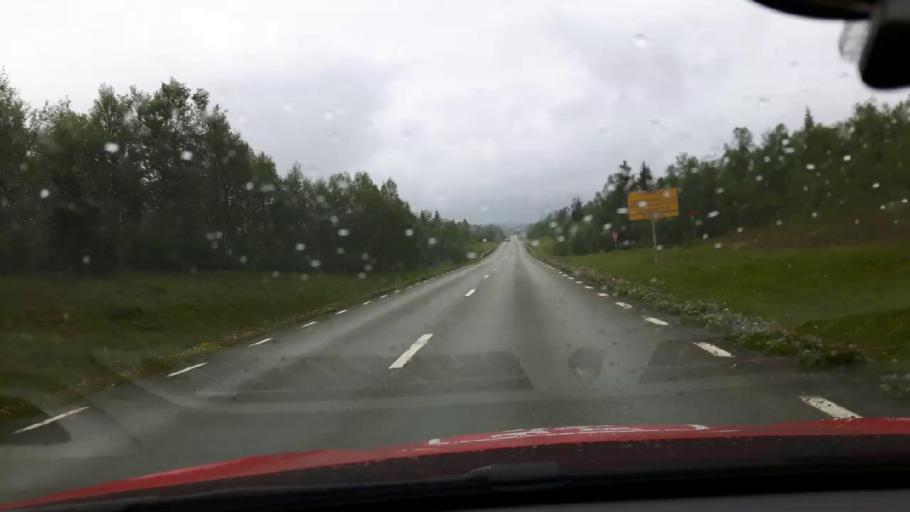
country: NO
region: Nord-Trondelag
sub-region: Meraker
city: Meraker
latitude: 63.2764
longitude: 12.1425
